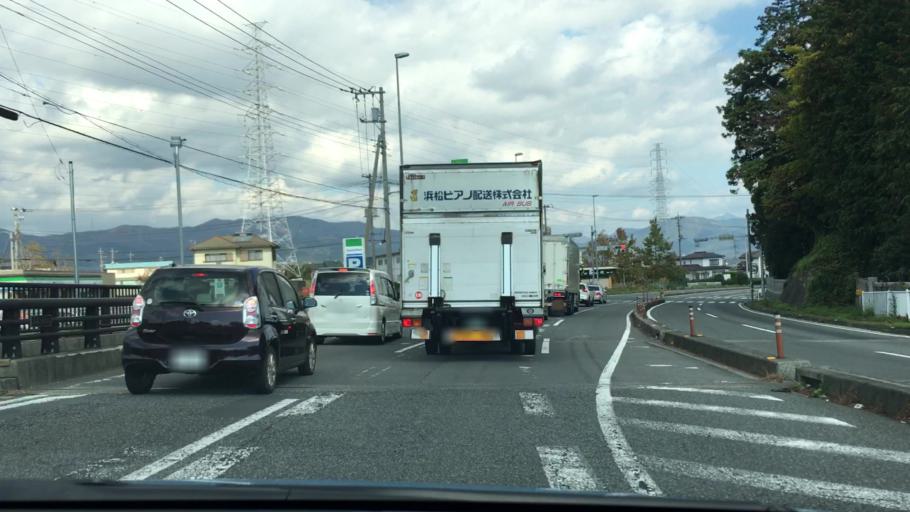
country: JP
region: Shizuoka
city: Gotemba
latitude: 35.3362
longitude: 138.9355
